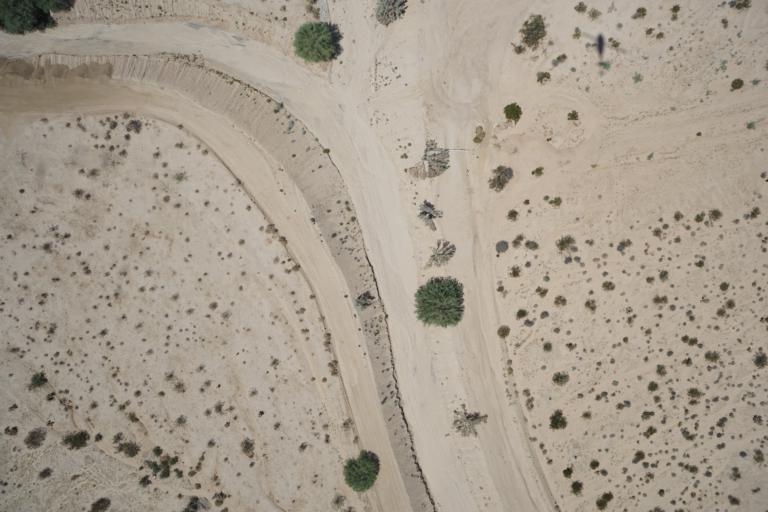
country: US
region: California
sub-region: San Bernardino County
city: Twentynine Palms
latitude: 34.1366
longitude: -116.0711
